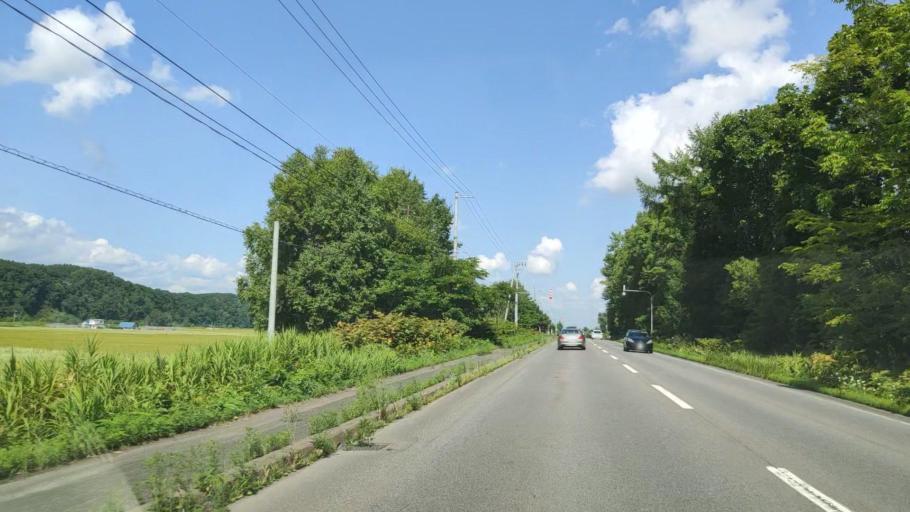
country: JP
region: Hokkaido
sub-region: Asahikawa-shi
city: Asahikawa
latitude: 43.6337
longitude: 142.4574
